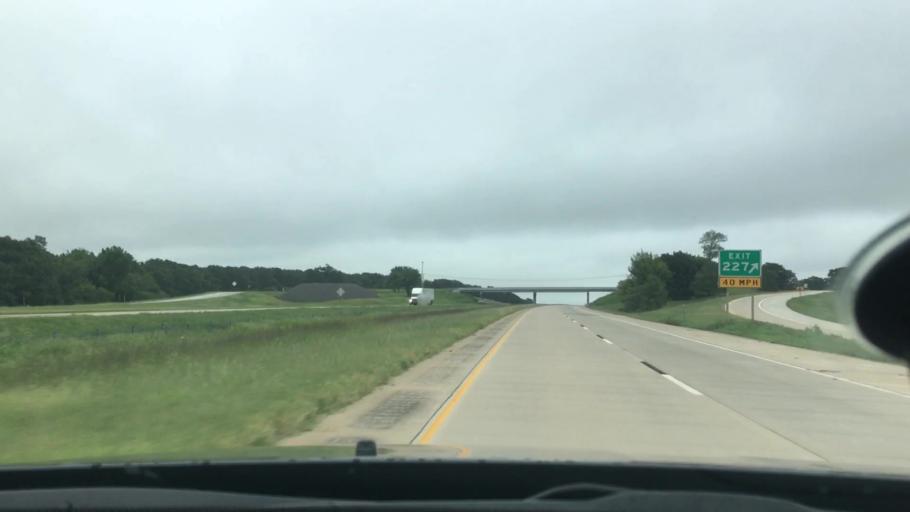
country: US
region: Oklahoma
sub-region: Okfuskee County
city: Okemah
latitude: 35.4301
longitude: -96.1981
